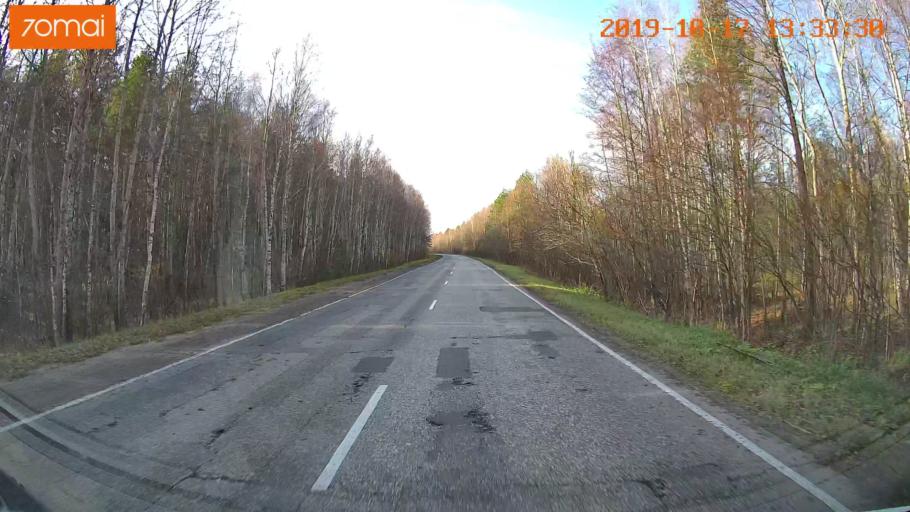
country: RU
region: Vladimir
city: Velikodvorskiy
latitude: 55.1429
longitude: 40.7400
